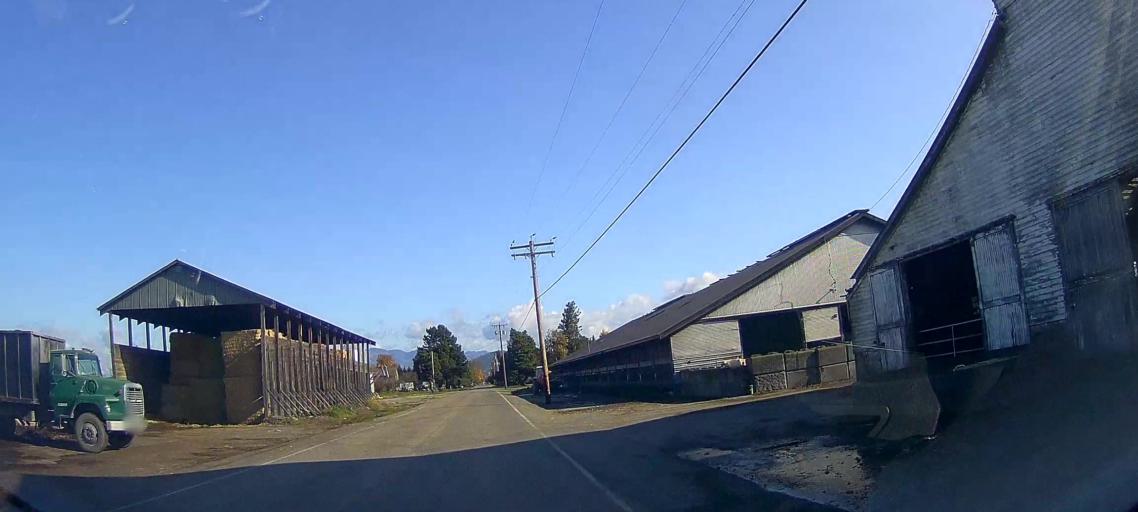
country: US
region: Washington
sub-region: Skagit County
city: Mount Vernon
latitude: 48.3993
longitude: -122.3991
